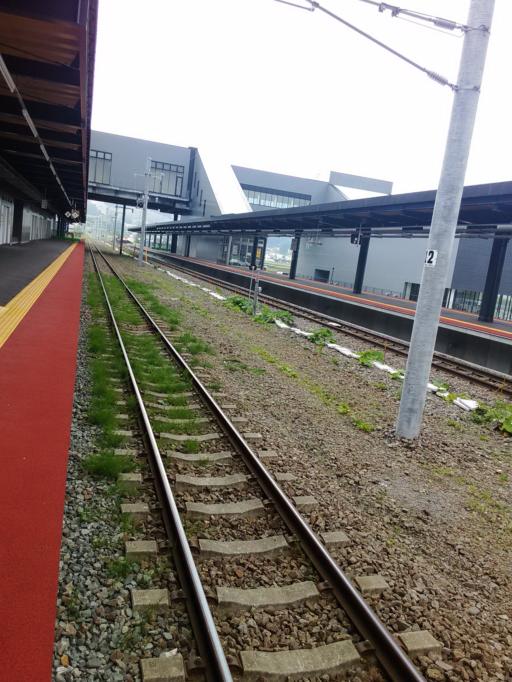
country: JP
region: Hokkaido
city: Nanae
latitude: 41.9047
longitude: 140.6493
